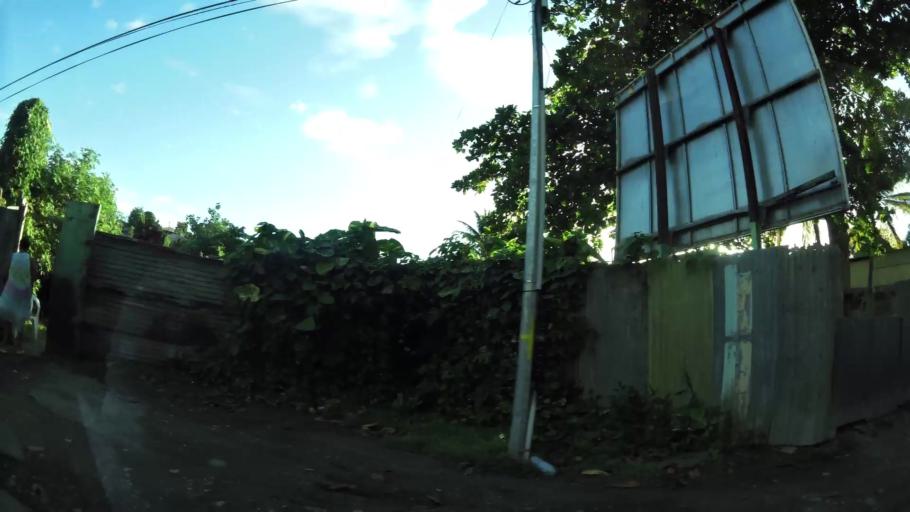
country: GP
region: Guadeloupe
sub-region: Guadeloupe
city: Pointe-a-Pitre
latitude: 16.2303
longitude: -61.5313
